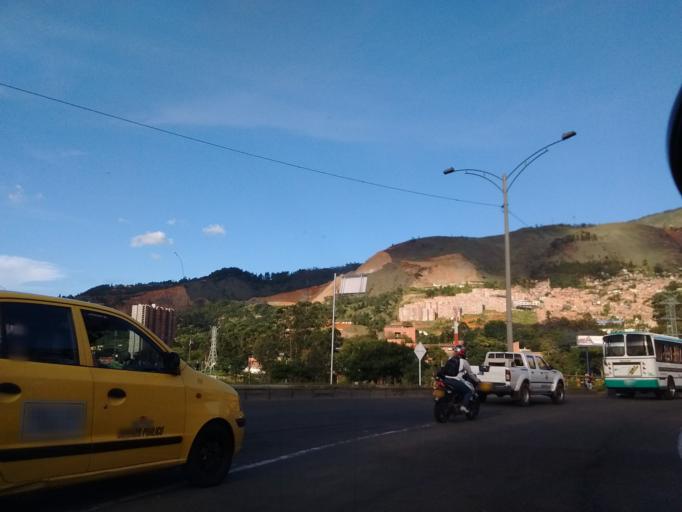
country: CO
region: Antioquia
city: Bello
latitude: 6.3109
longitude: -75.5580
